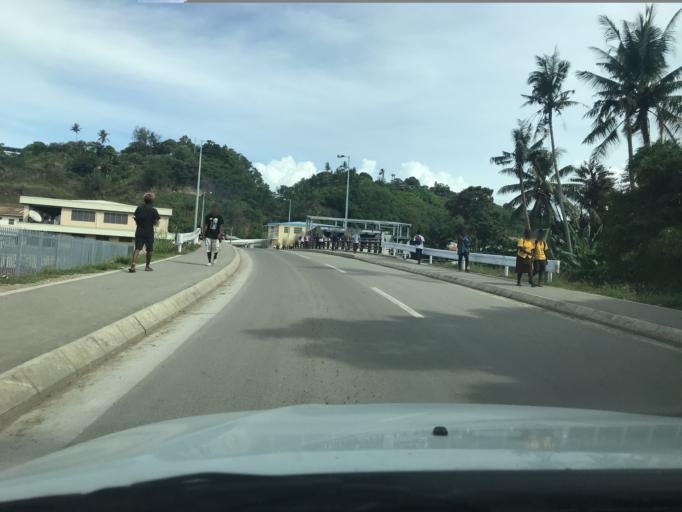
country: SB
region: Guadalcanal
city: Honiara
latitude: -9.4378
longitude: 159.9637
